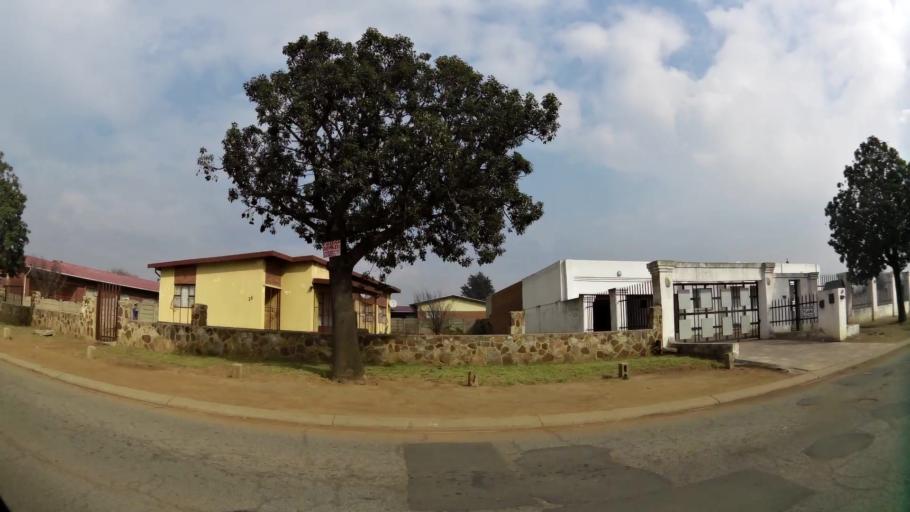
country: ZA
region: Gauteng
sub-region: Sedibeng District Municipality
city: Vanderbijlpark
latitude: -26.6796
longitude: 27.8389
